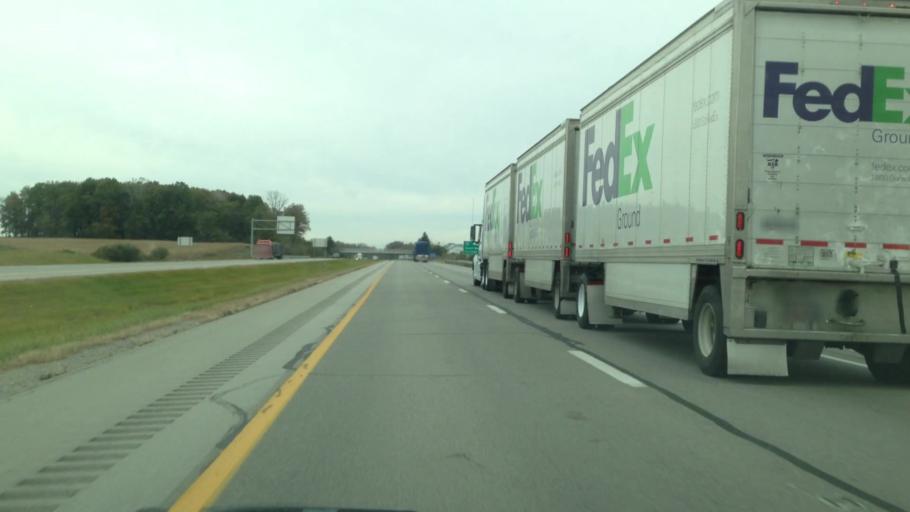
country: US
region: Indiana
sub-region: Steuben County
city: Hamilton
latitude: 41.6305
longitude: -84.7802
